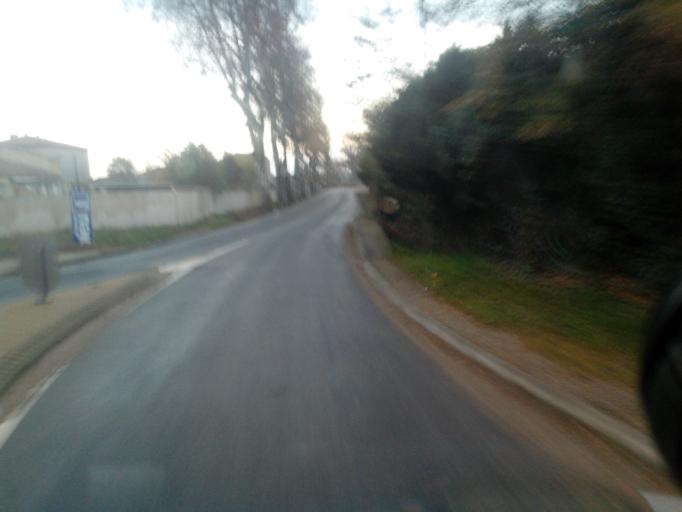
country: FR
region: Languedoc-Roussillon
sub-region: Departement de l'Herault
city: Aniane
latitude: 43.6806
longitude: 3.5786
